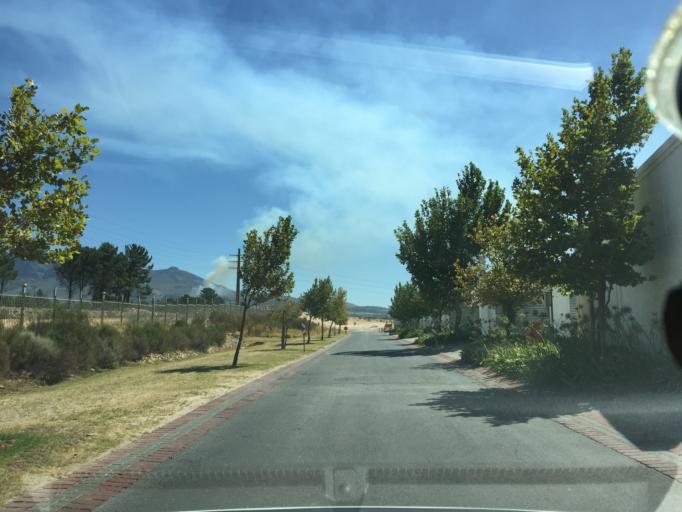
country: ZA
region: Western Cape
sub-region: Cape Winelands District Municipality
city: Paarl
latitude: -33.8085
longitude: 18.9757
